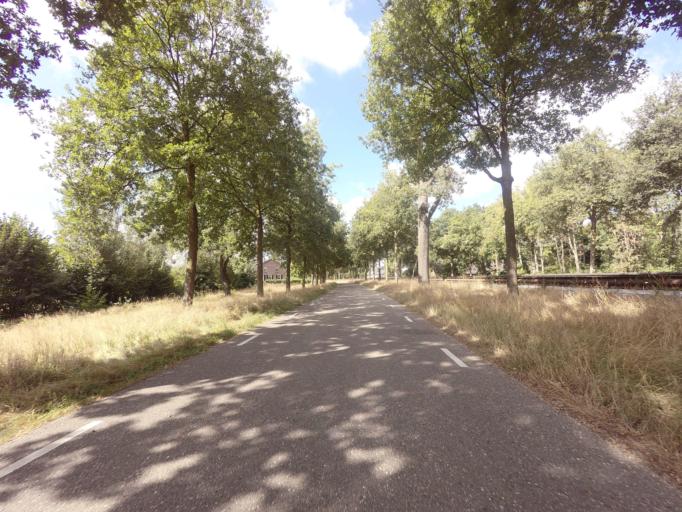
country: NL
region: North Brabant
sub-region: Gemeente Landerd
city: Schaijk
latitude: 51.7371
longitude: 5.6271
